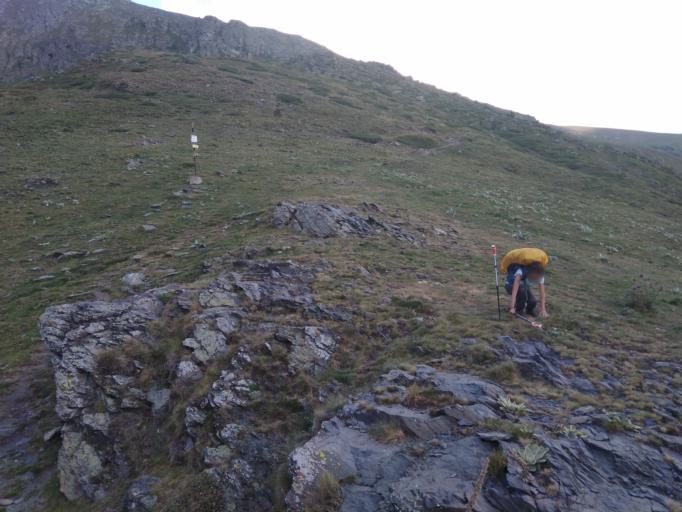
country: BG
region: Plovdiv
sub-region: Obshtina Karlovo
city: Karlovo
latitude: 42.7036
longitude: 24.8607
